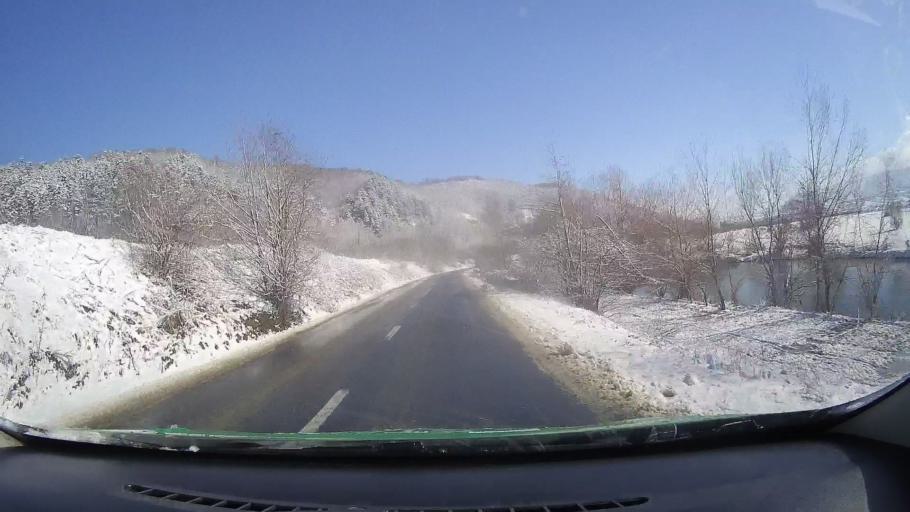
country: RO
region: Sibiu
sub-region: Comuna Talmaciu
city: Talmaciu
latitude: 45.6604
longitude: 24.2790
